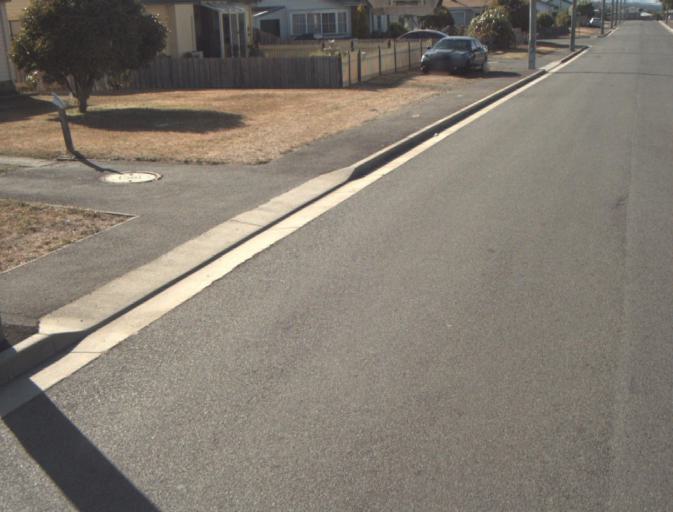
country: AU
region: Tasmania
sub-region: Launceston
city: Mayfield
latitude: -41.3886
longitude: 147.1333
